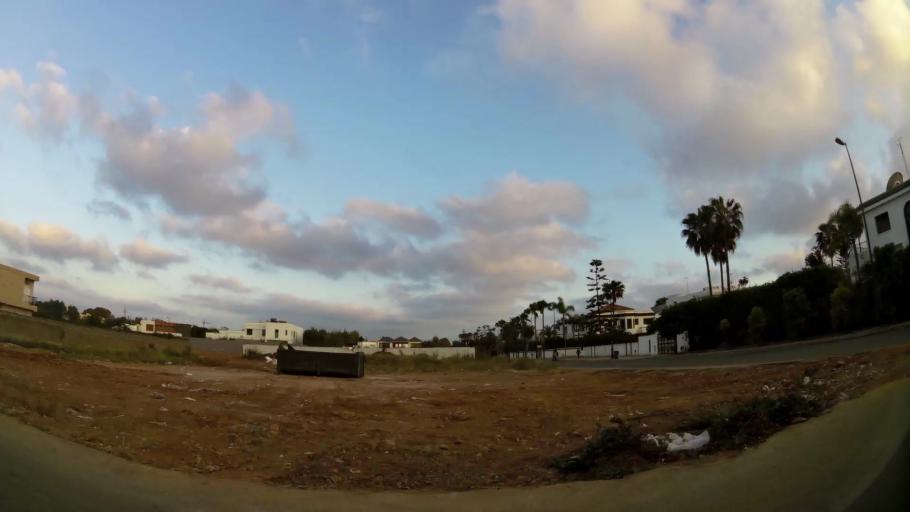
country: MA
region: Rabat-Sale-Zemmour-Zaer
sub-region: Rabat
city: Rabat
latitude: 33.9713
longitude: -6.8340
